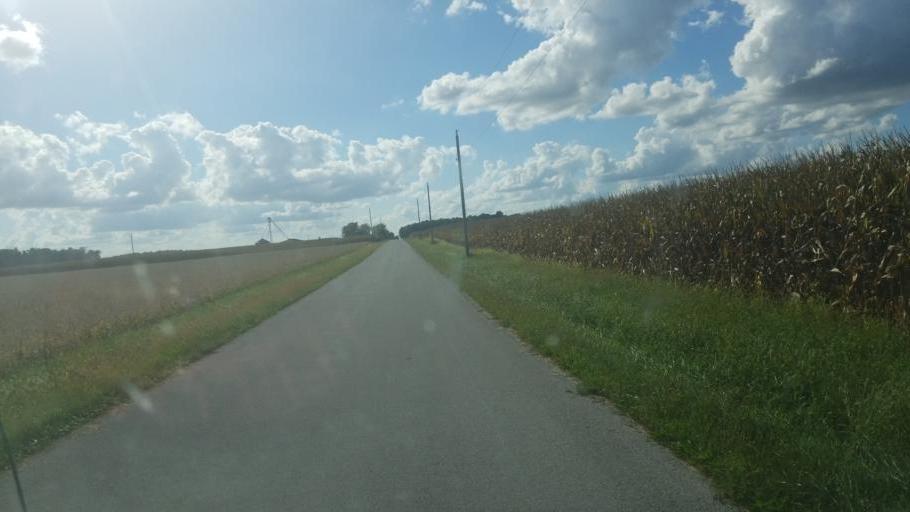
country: US
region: Ohio
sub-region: Hardin County
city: Kenton
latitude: 40.7182
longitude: -83.7084
